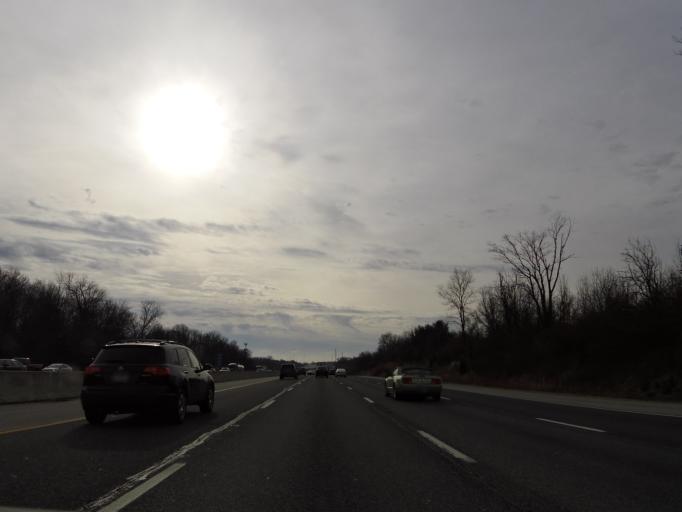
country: US
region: Indiana
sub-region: Marion County
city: Lawrence
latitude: 39.8735
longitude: -86.0475
